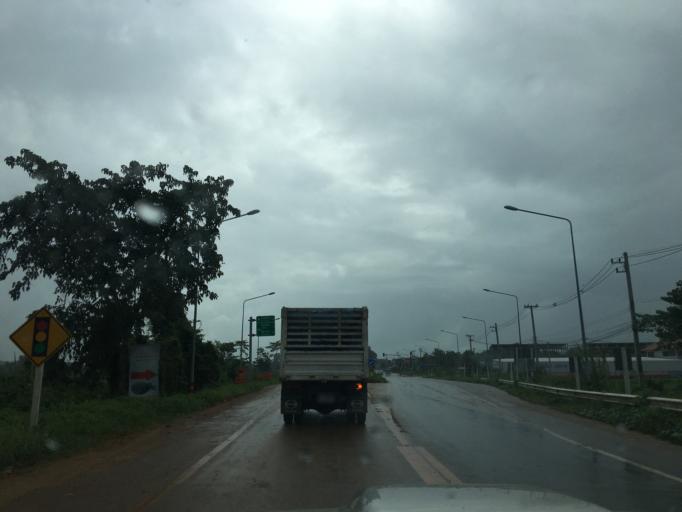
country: TH
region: Chiang Rai
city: Chiang Rai
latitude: 20.0053
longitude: 99.8911
